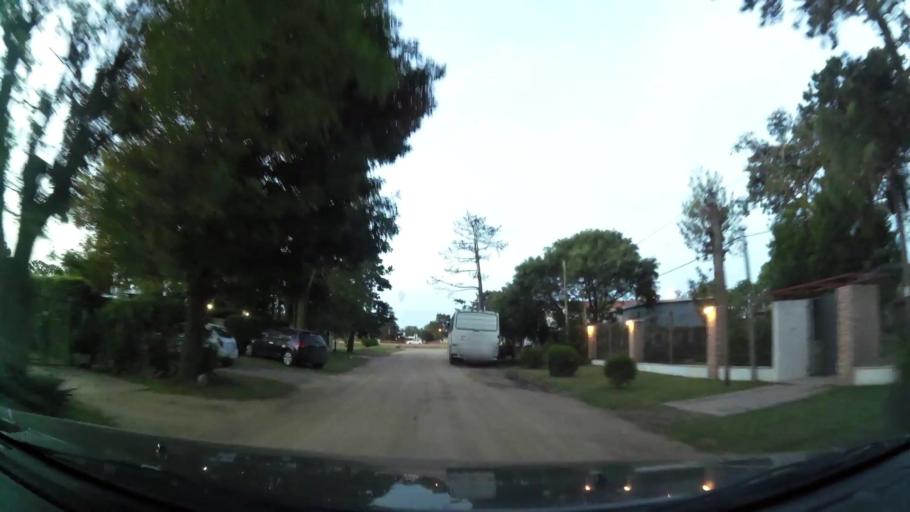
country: UY
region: Canelones
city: Atlantida
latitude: -34.7667
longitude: -55.7579
